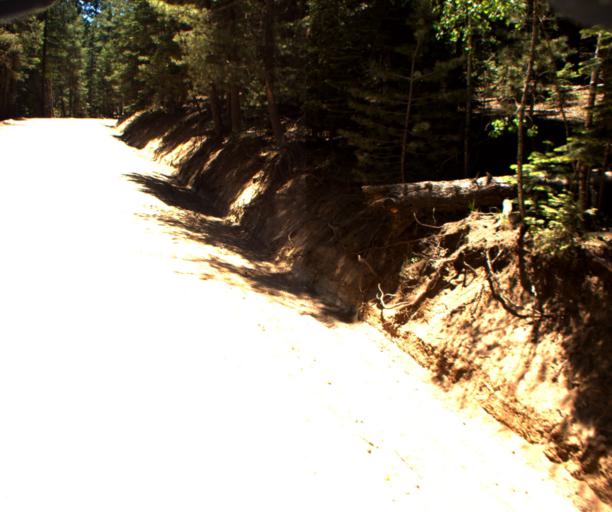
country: US
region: Arizona
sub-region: Graham County
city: Swift Trail Junction
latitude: 32.6694
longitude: -109.8791
